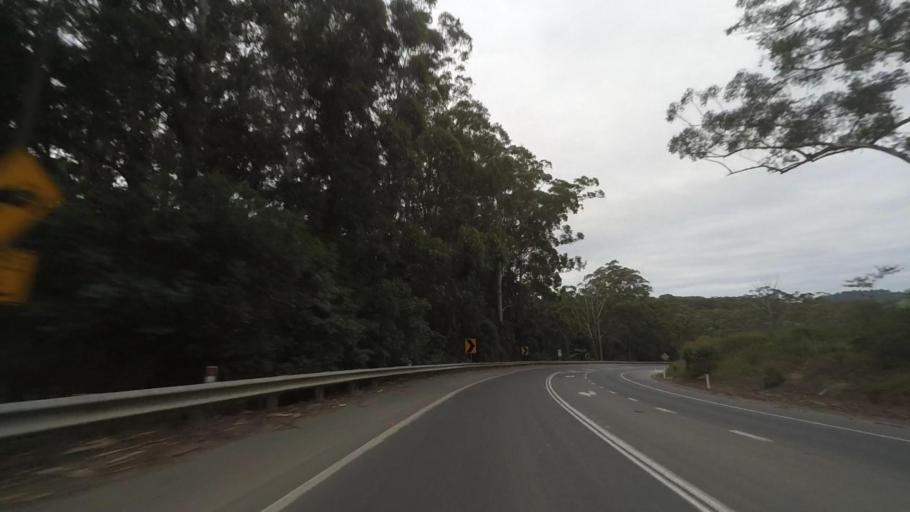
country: AU
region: New South Wales
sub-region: Shoalhaven Shire
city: Berry
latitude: -34.7625
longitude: 150.7253
